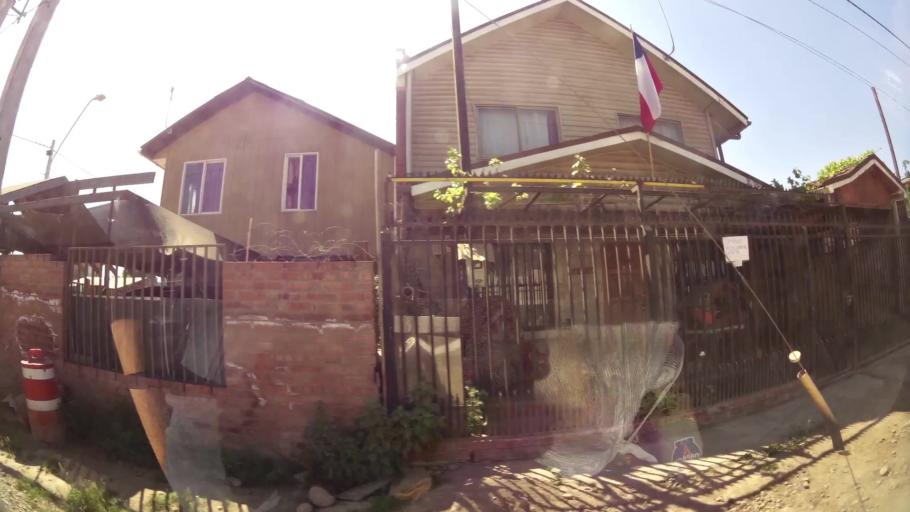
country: CL
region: Santiago Metropolitan
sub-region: Provincia de Talagante
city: Penaflor
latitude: -33.5841
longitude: -70.8070
